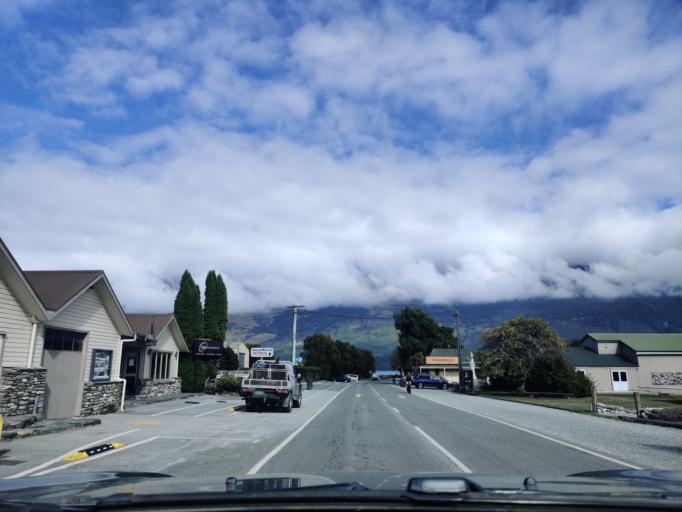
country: NZ
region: Otago
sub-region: Queenstown-Lakes District
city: Queenstown
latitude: -44.8497
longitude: 168.3851
